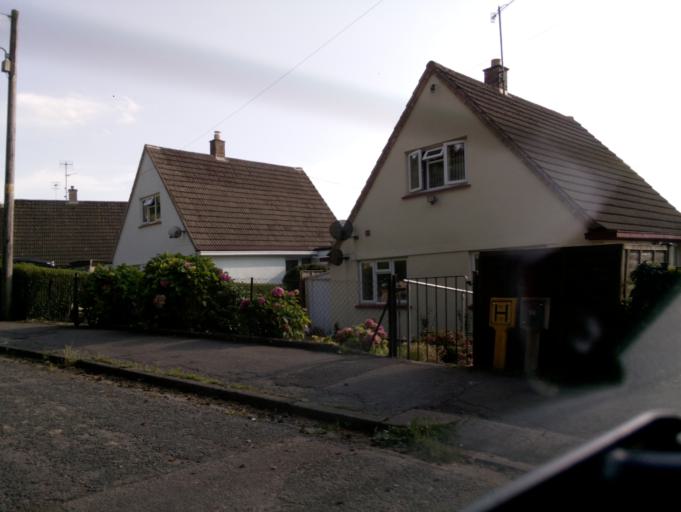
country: GB
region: England
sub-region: Gloucestershire
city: Stroud
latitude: 51.7361
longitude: -2.2276
